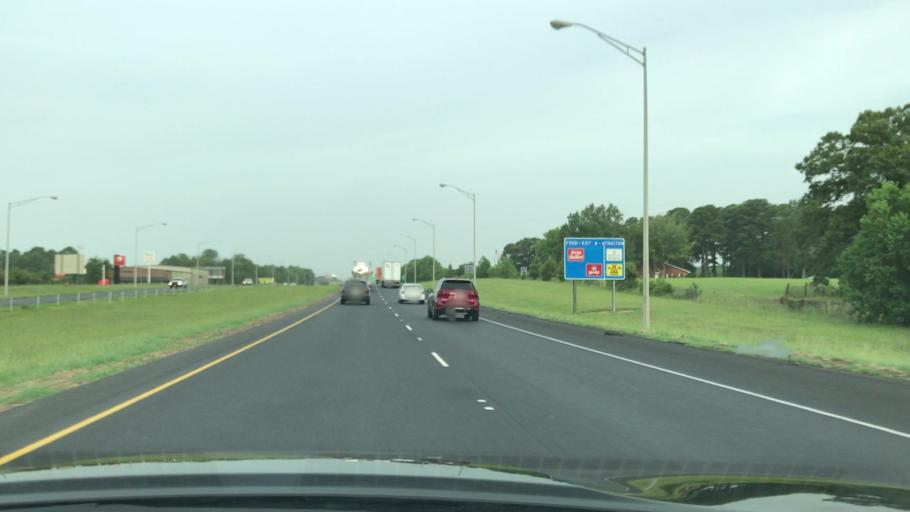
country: US
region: Louisiana
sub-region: Caddo Parish
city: Greenwood
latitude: 32.4496
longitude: -93.8879
